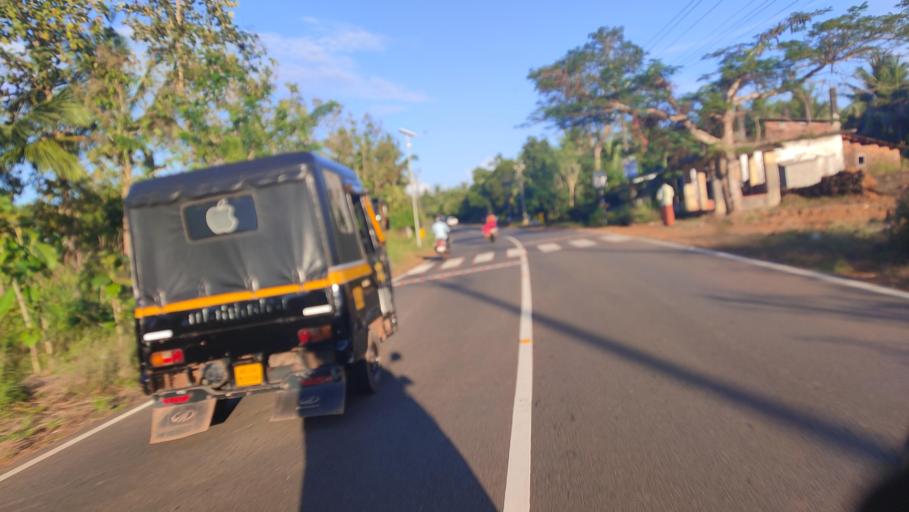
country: IN
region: Kerala
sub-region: Kasaragod District
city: Kasaragod
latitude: 12.4651
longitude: 75.0753
